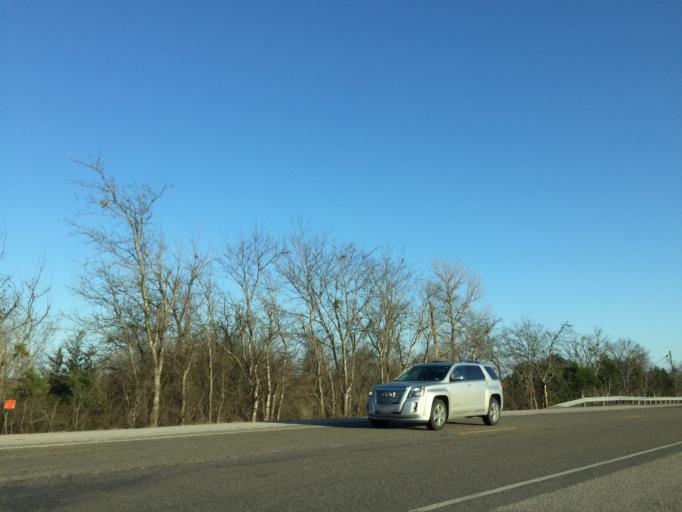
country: US
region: Texas
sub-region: Williamson County
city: Florence
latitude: 30.7536
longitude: -97.8075
